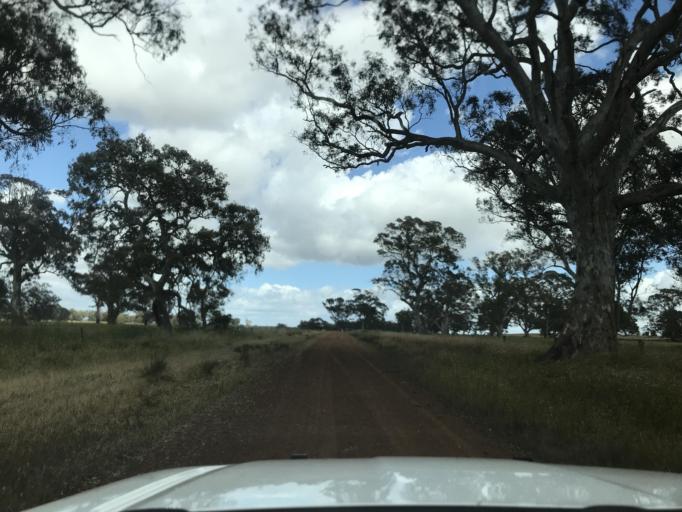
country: AU
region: South Australia
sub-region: Wattle Range
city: Penola
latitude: -37.1901
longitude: 141.4340
